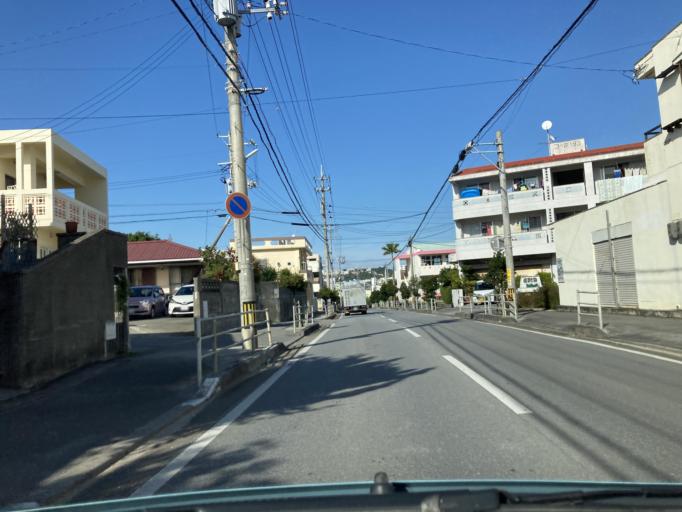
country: JP
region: Okinawa
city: Tomigusuku
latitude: 26.1836
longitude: 127.7070
